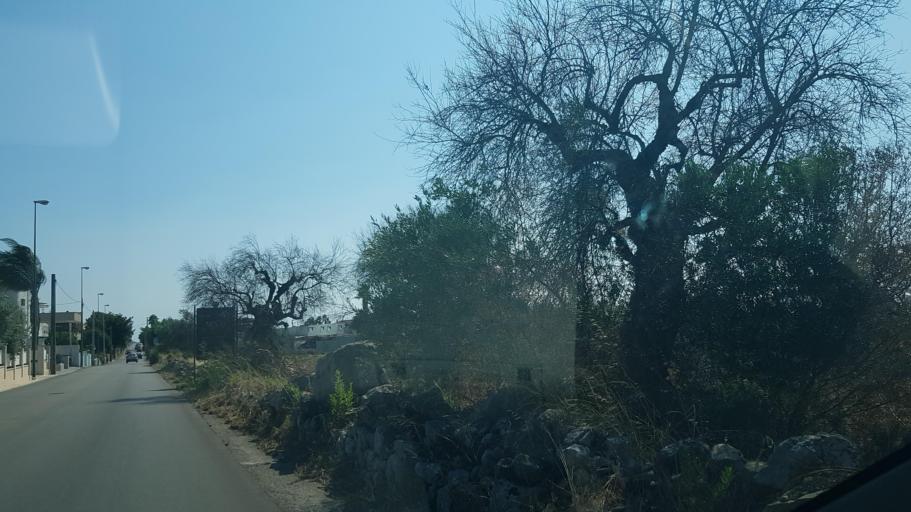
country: IT
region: Apulia
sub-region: Provincia di Lecce
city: Ugento
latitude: 39.9195
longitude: 18.1549
